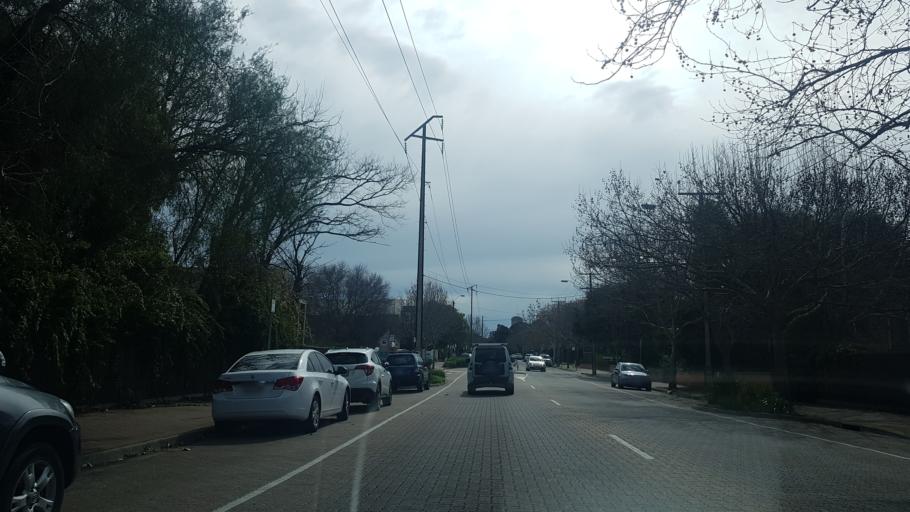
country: AU
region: South Australia
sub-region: Unley
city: Unley
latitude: -34.9466
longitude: 138.5994
